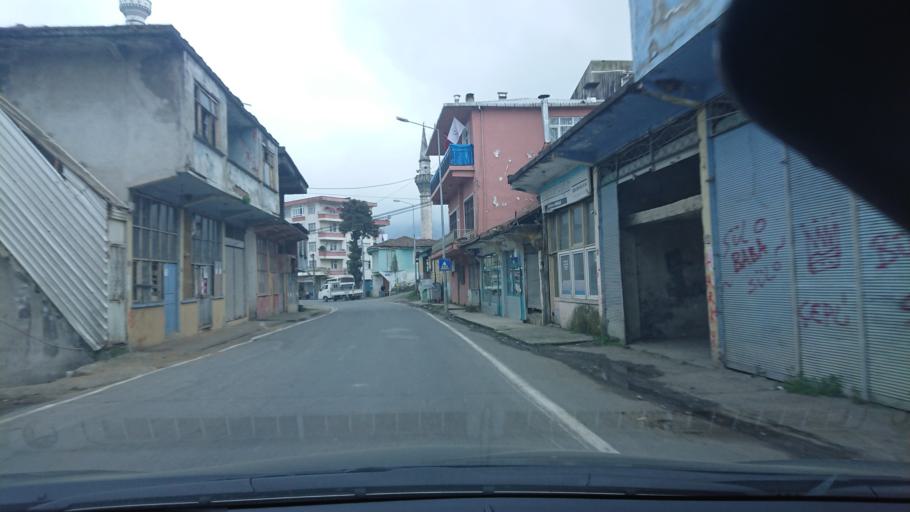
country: TR
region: Rize
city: Rize
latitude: 40.9997
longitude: 40.4874
